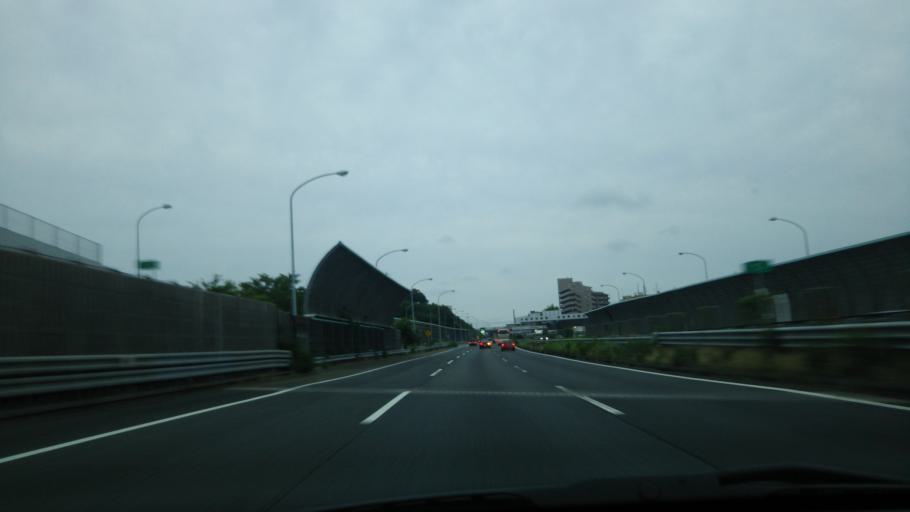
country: JP
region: Tokyo
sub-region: Machida-shi
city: Machida
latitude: 35.5446
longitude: 139.5406
